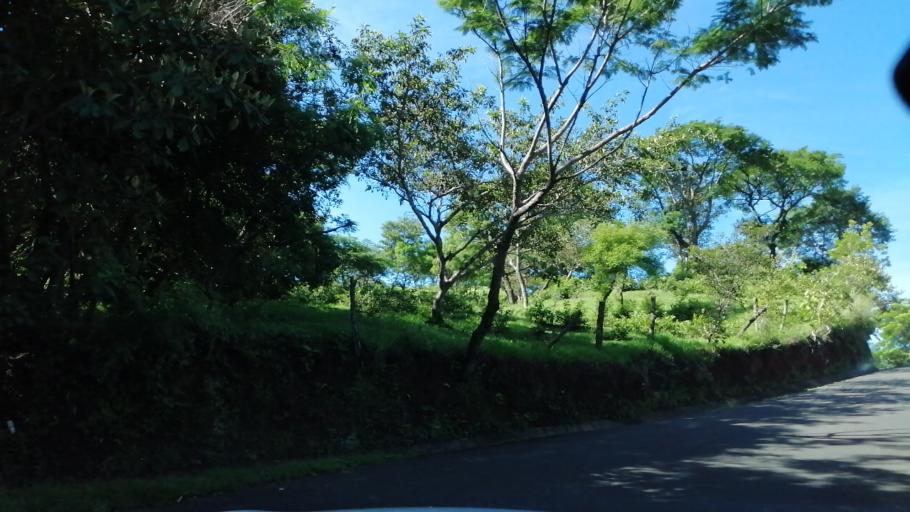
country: SV
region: Morazan
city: Corinto
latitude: 13.8118
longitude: -87.9800
